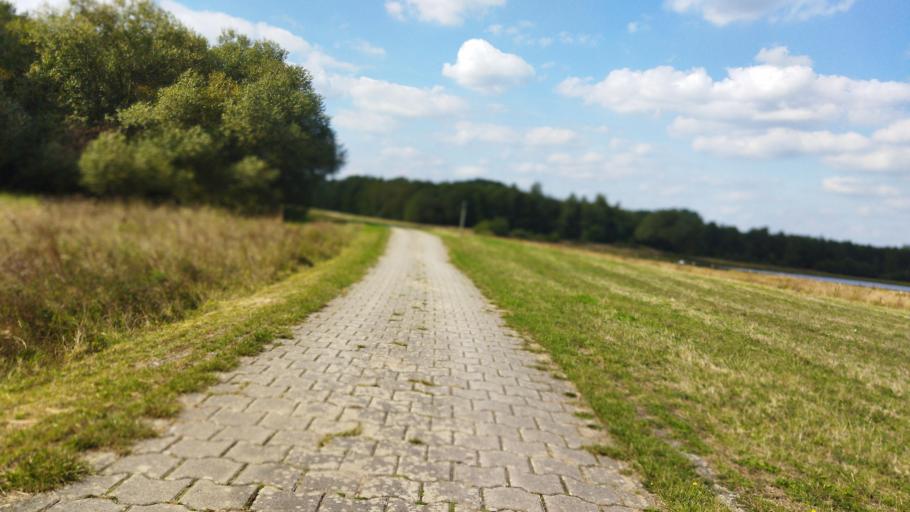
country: DE
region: Lower Saxony
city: Haren
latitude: 52.7821
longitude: 7.2602
